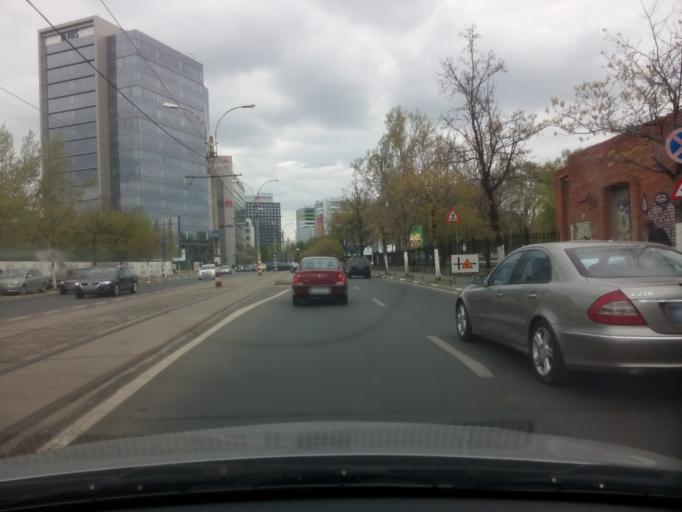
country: RO
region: Bucuresti
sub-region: Municipiul Bucuresti
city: Bucharest
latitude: 44.4747
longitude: 26.1075
